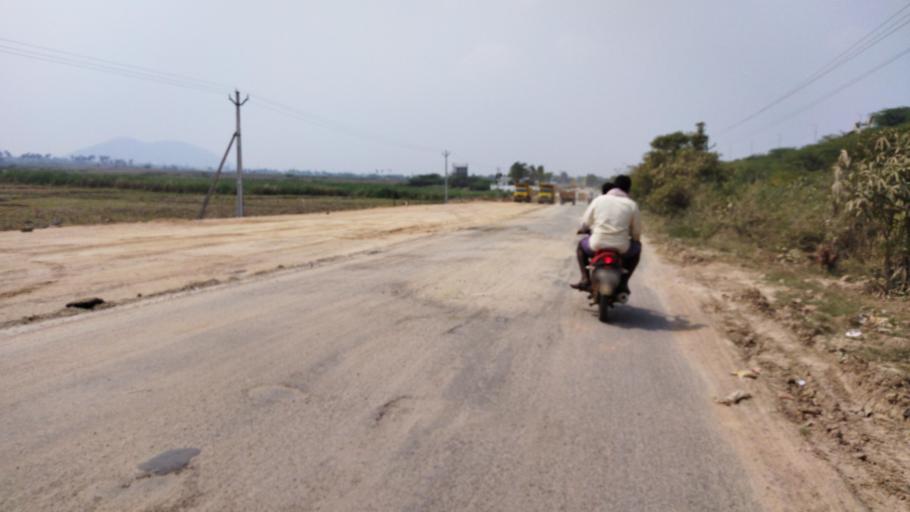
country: IN
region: Telangana
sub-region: Nalgonda
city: Nalgonda
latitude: 17.0790
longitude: 79.3073
